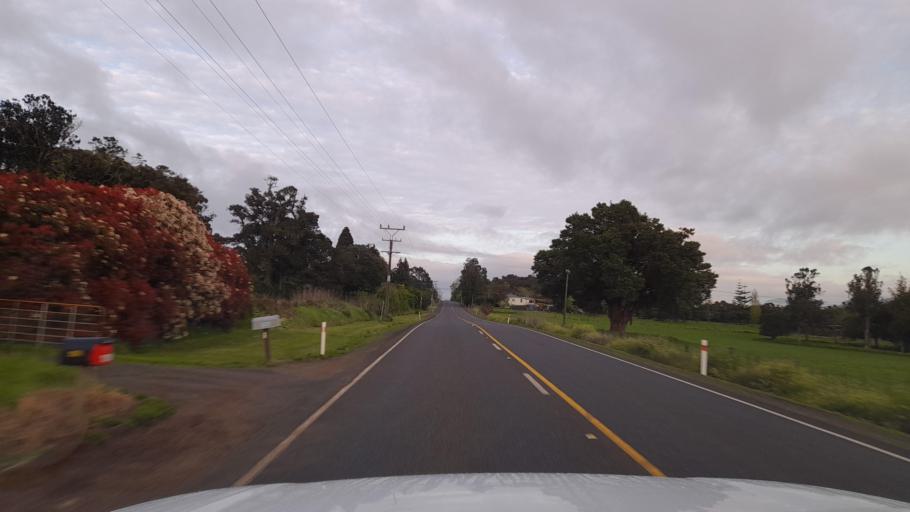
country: NZ
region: Northland
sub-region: Whangarei
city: Maungatapere
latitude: -35.7501
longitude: 174.1656
